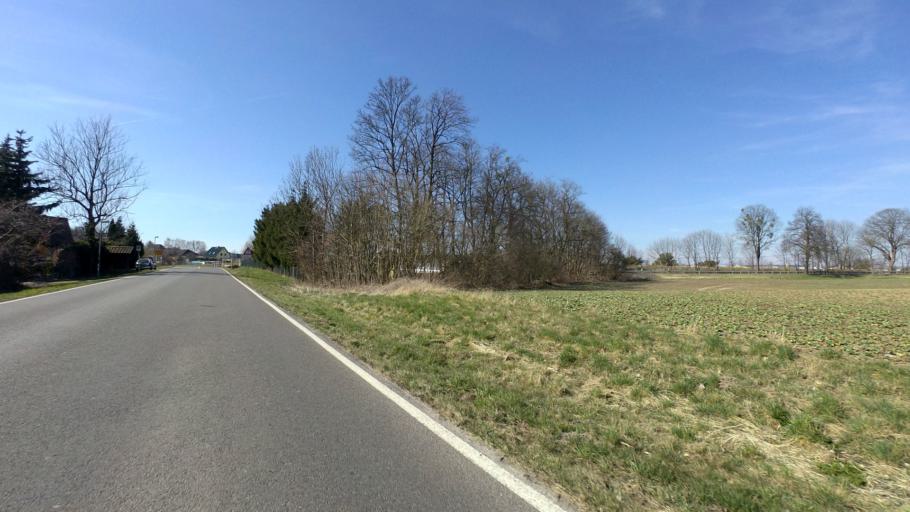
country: DE
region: Brandenburg
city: Protzel
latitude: 52.6375
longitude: 13.9930
